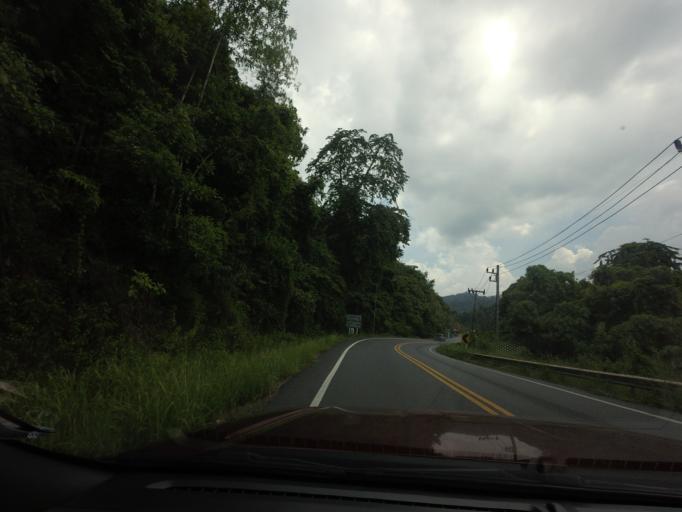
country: TH
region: Yala
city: Than To
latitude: 6.0466
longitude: 101.1989
